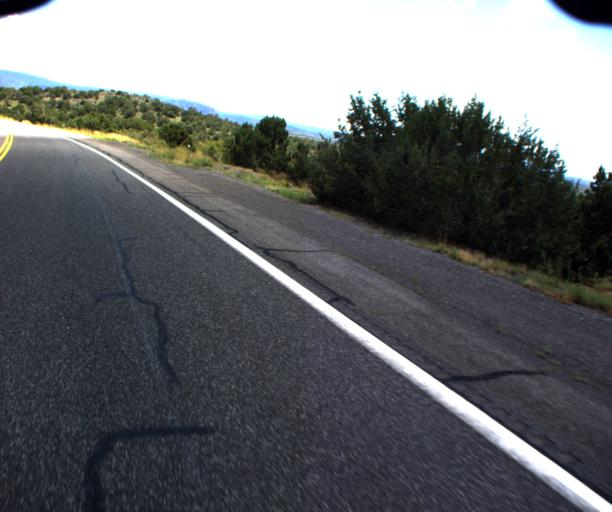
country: US
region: Arizona
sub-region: Gila County
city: Pine
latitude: 34.4869
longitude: -111.6229
